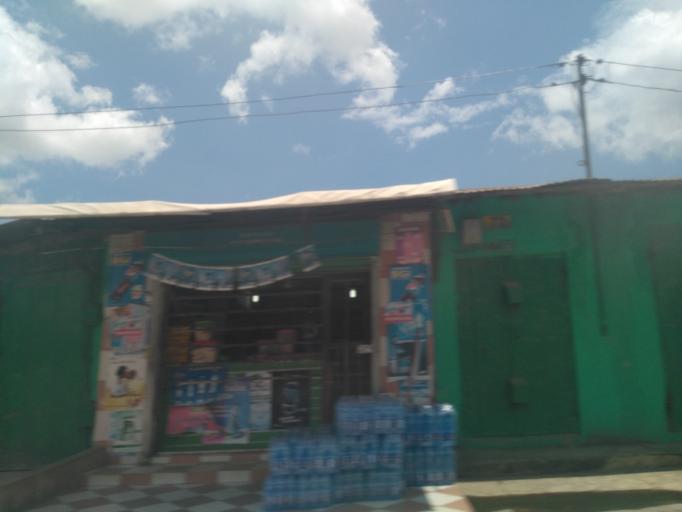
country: TZ
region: Dar es Salaam
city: Dar es Salaam
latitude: -6.8601
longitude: 39.2639
